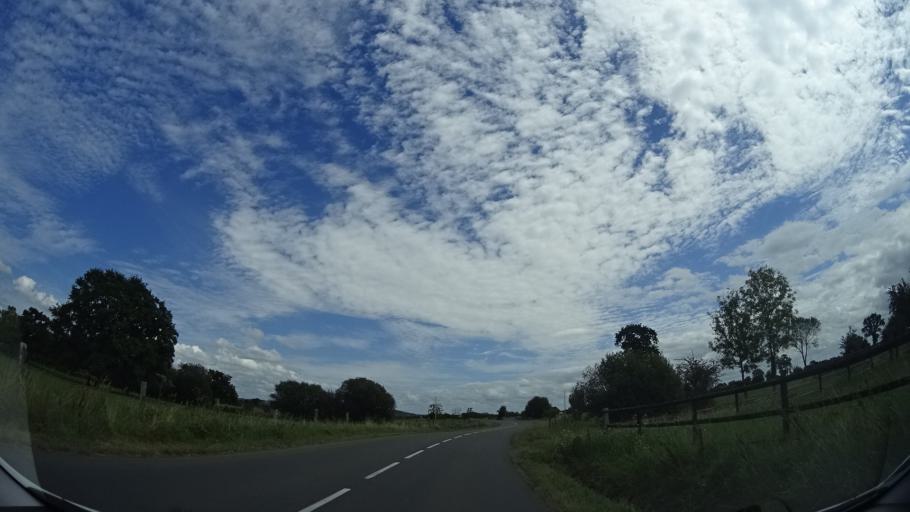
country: FR
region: Lower Normandy
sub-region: Departement de la Manche
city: Marcey-les-Greves
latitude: 48.6872
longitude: -1.4360
